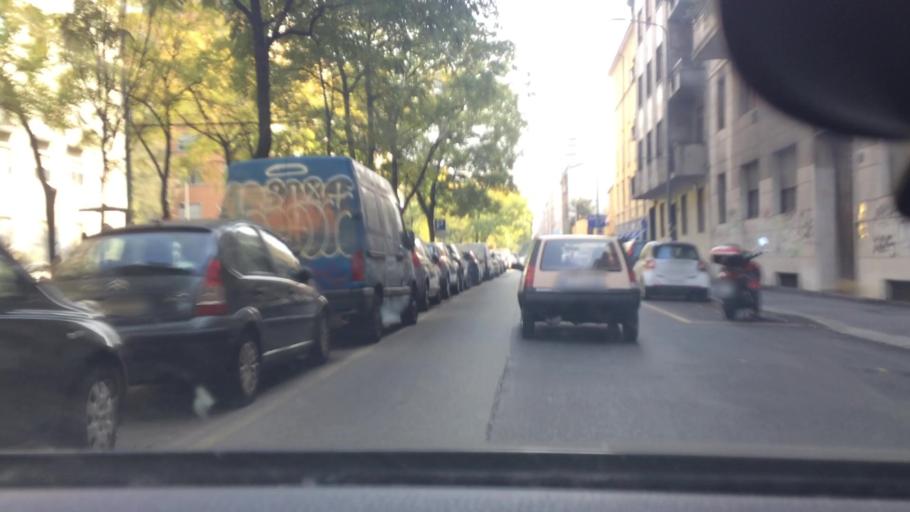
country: IT
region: Lombardy
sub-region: Citta metropolitana di Milano
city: Milano
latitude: 45.4757
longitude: 9.2087
